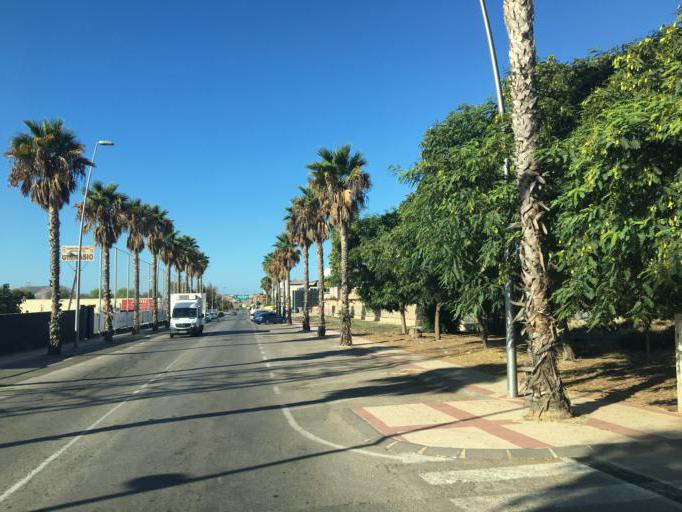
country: ES
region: Murcia
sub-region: Murcia
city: Cartagena
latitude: 37.6218
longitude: -0.9497
